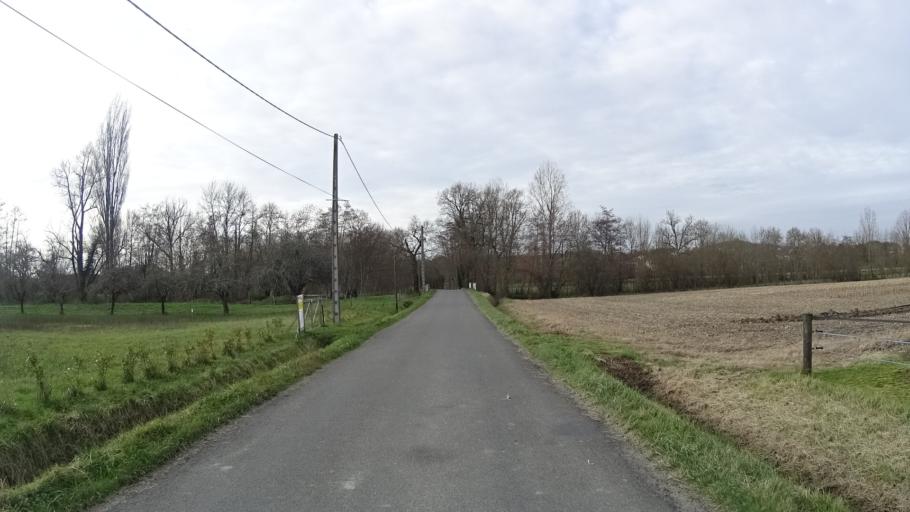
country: FR
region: Aquitaine
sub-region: Departement de la Dordogne
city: Saint-Aulaye
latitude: 45.2391
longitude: 0.1573
